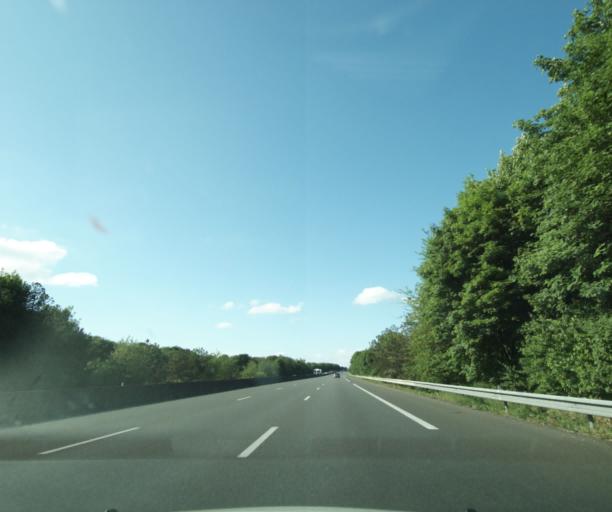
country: FR
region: Centre
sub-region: Departement d'Eure-et-Loir
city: Baigneaux
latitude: 48.1621
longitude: 1.8542
